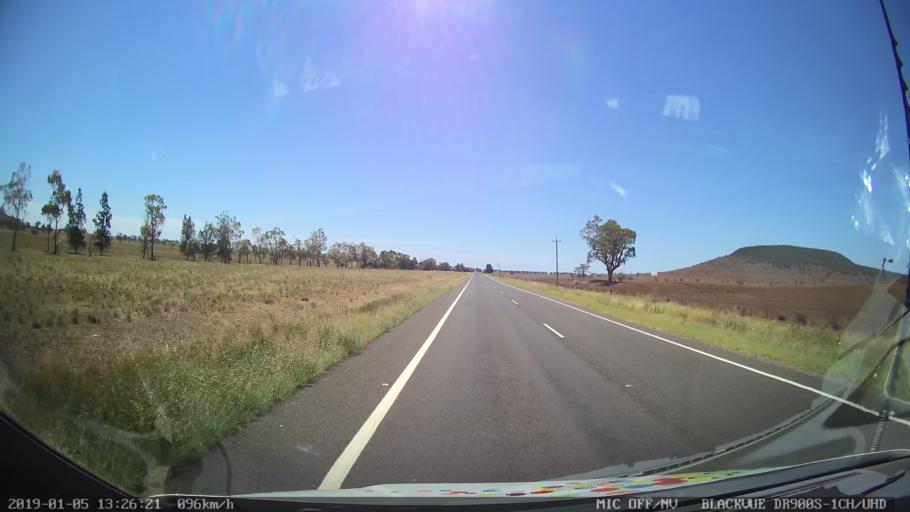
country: AU
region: New South Wales
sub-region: Gunnedah
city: Gunnedah
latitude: -31.0537
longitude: 150.0144
